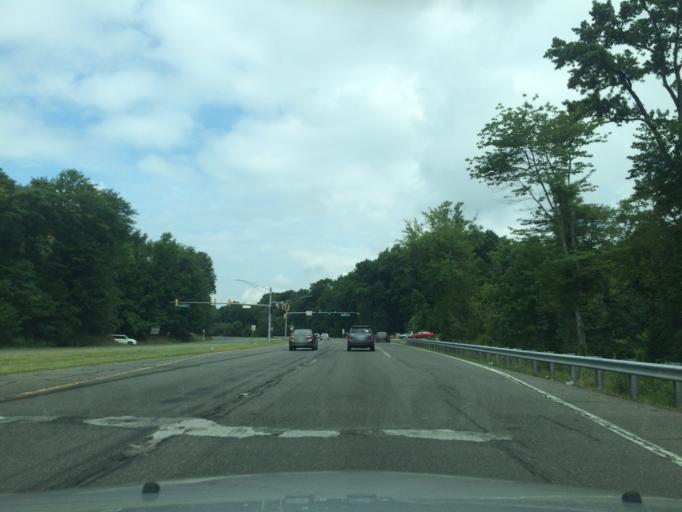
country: US
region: Maryland
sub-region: Prince George's County
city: Coral Hills
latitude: 38.8641
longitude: -76.9234
